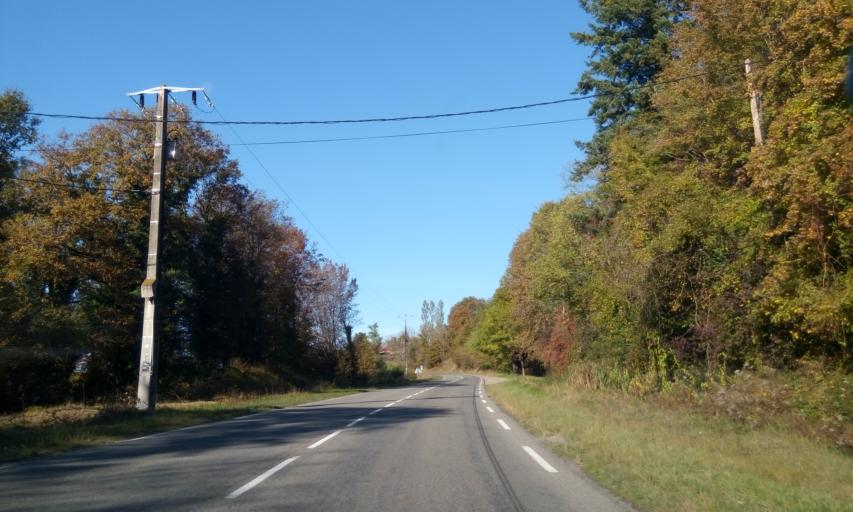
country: FR
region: Rhone-Alpes
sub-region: Departement du Rhone
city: Bourg-de-Thizy
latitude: 46.0324
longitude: 4.2508
